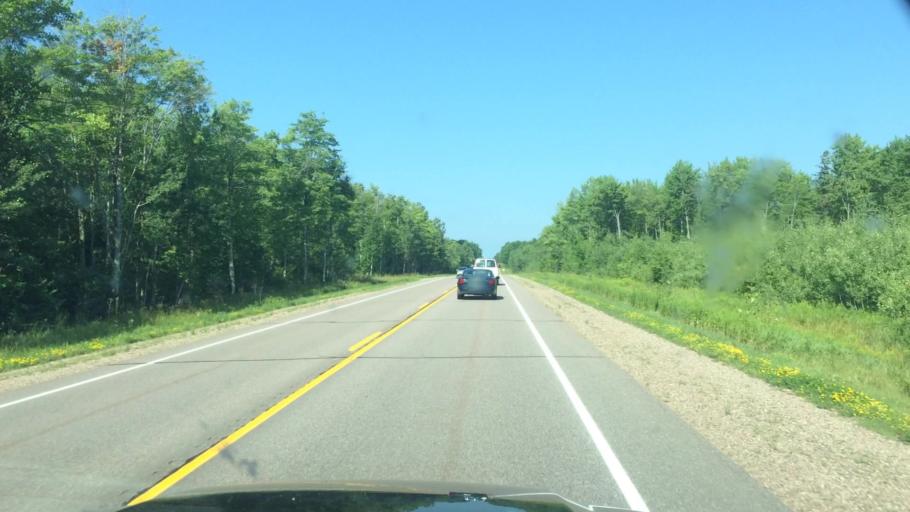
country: US
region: Wisconsin
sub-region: Langlade County
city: Antigo
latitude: 45.1469
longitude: -89.3732
